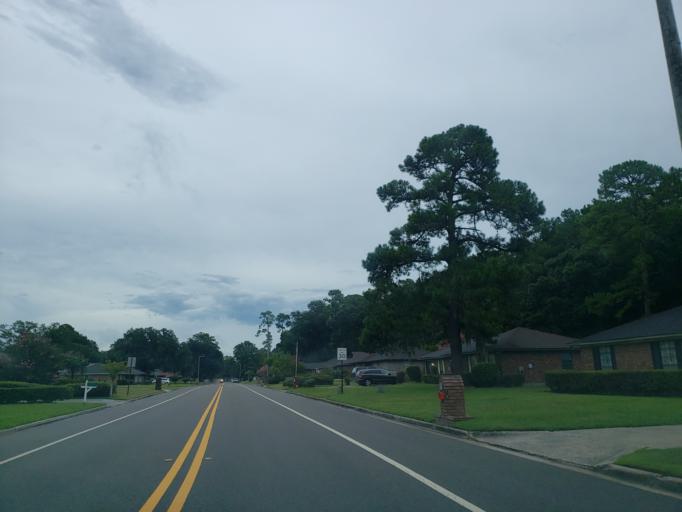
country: US
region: Georgia
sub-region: Chatham County
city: Isle of Hope
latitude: 31.9995
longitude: -81.0705
